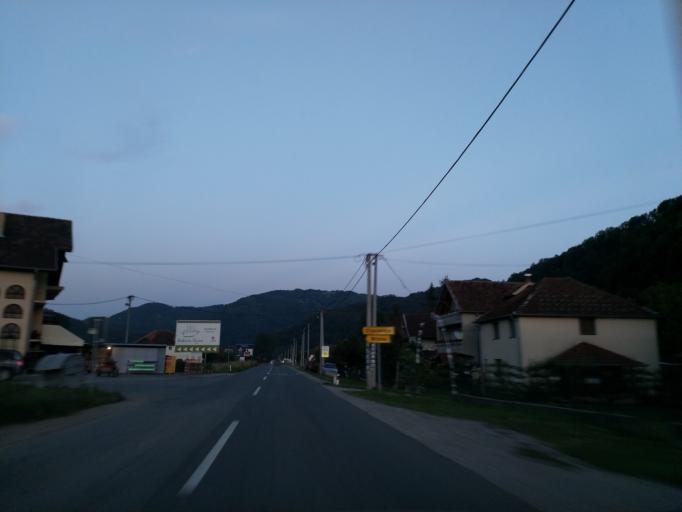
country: RS
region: Central Serbia
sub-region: Rasinski Okrug
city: Aleksandrovac
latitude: 43.3539
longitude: 21.0774
